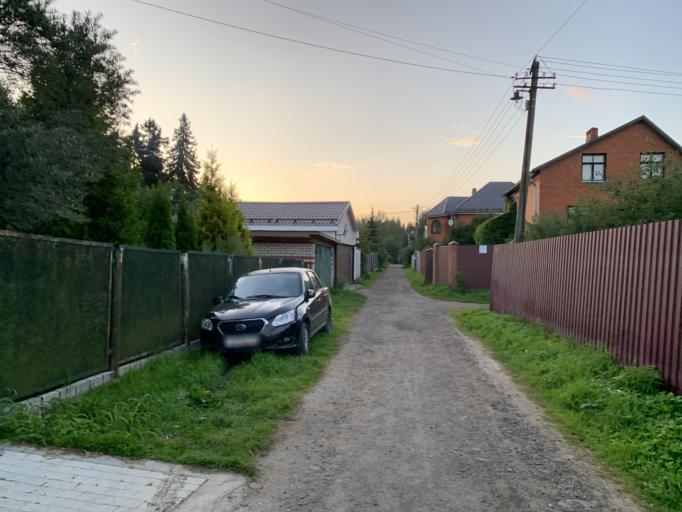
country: RU
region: Moskovskaya
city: Podosinki
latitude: 56.1756
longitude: 37.5778
